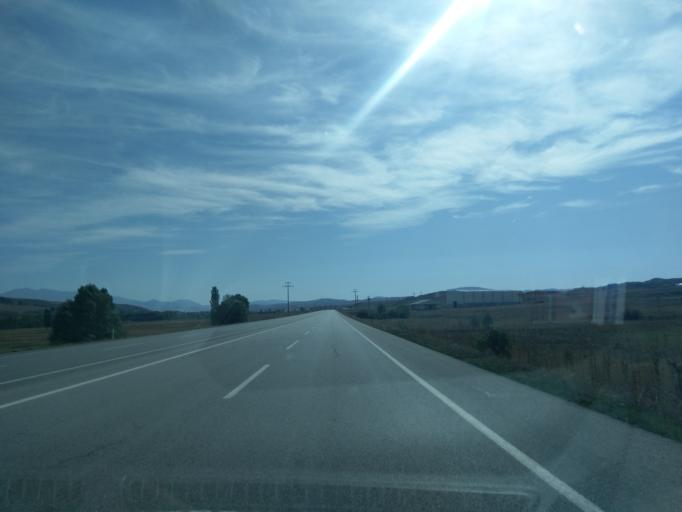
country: TR
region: Sivas
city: Imranli
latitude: 39.8747
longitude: 38.0822
